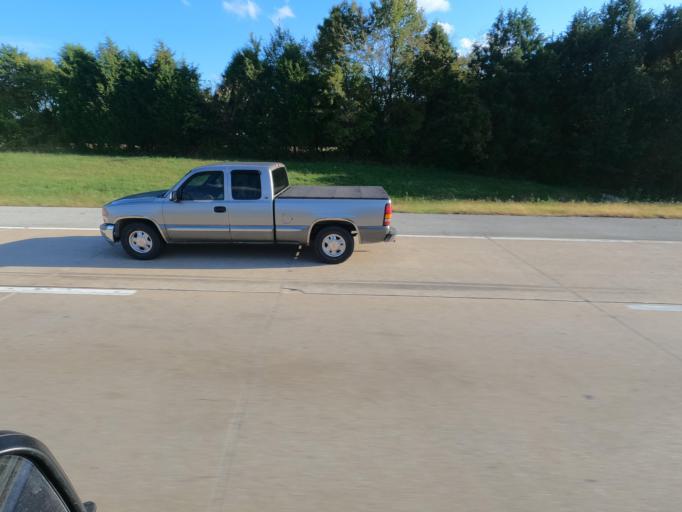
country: US
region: Tennessee
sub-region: Gibson County
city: Medina
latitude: 35.7191
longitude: -88.6305
